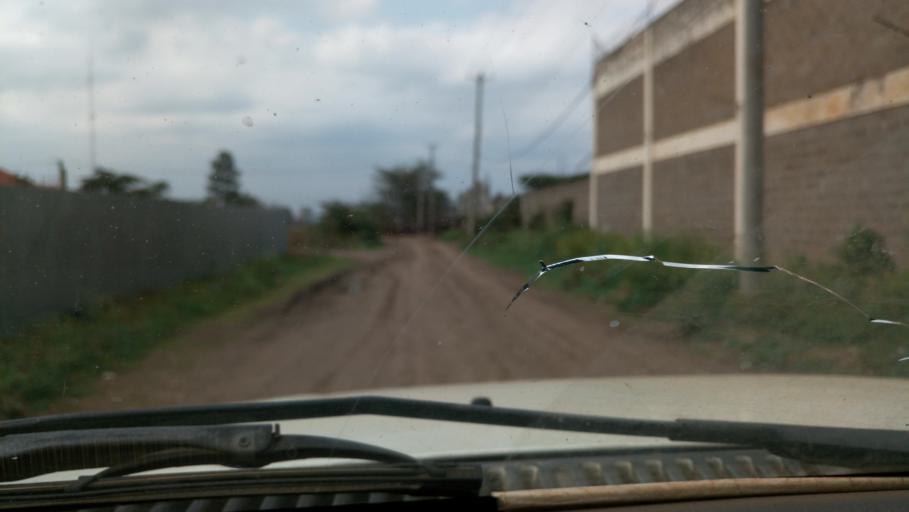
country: KE
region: Nairobi Area
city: Pumwani
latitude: -1.3237
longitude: 36.8506
